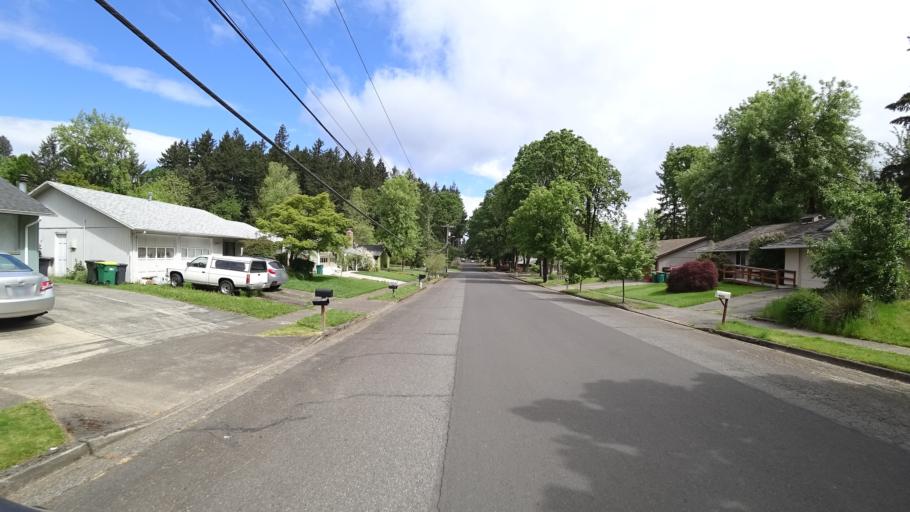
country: US
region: Oregon
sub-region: Washington County
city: Beaverton
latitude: 45.4712
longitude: -122.8107
